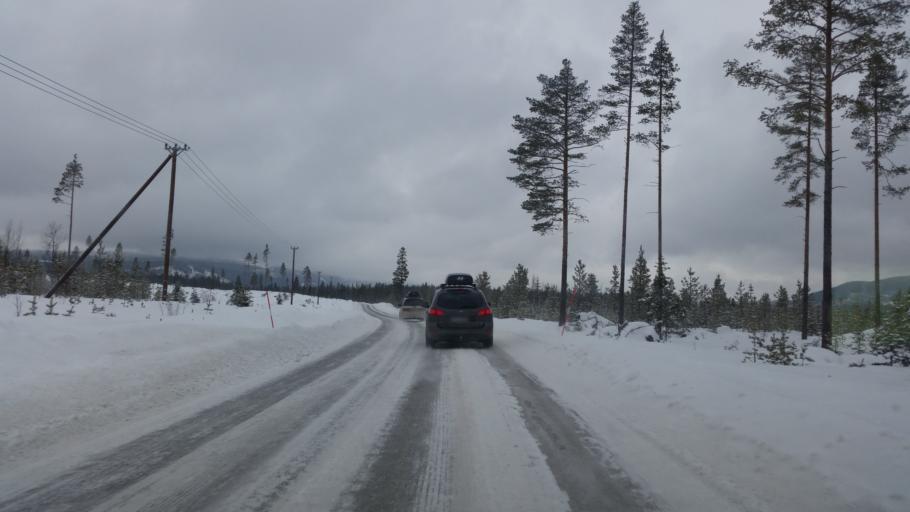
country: SE
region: Jaemtland
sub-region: Bergs Kommun
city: Hoverberg
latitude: 62.4749
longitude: 14.2591
